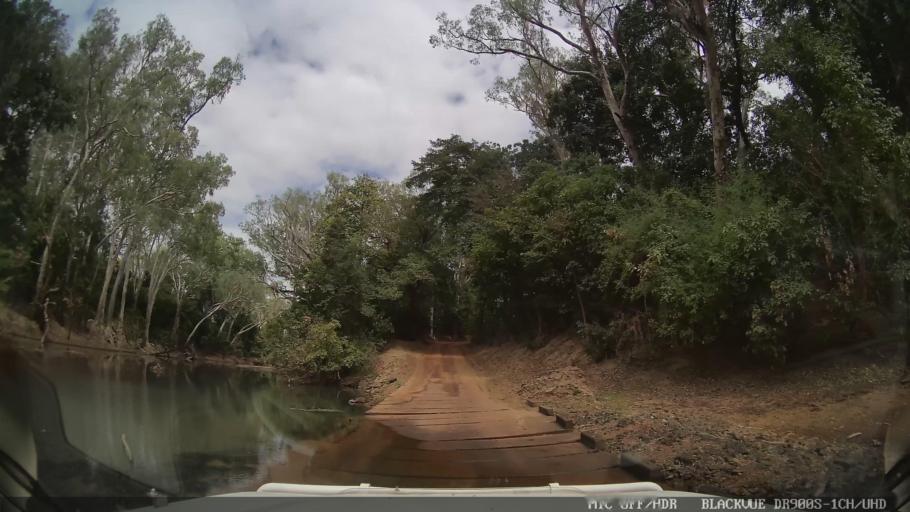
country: AU
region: Queensland
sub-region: Cook
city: Cooktown
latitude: -15.2902
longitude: 144.8446
